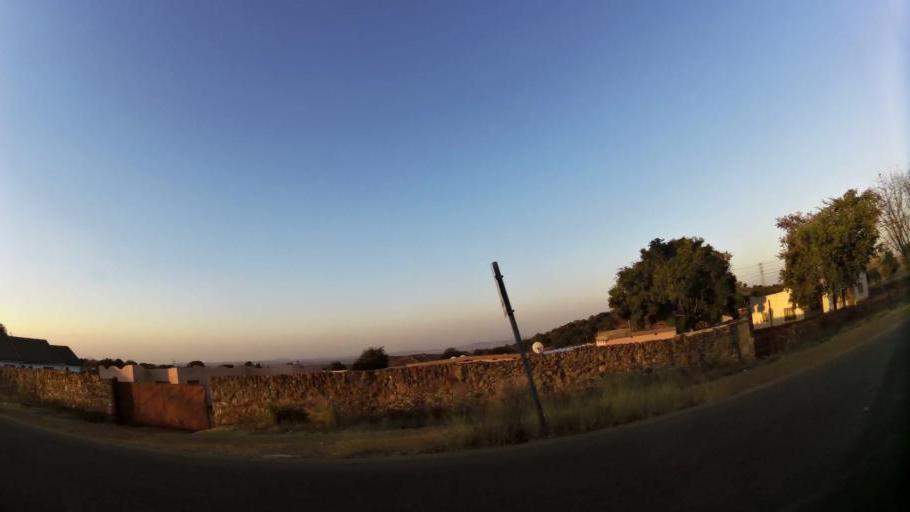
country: ZA
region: North-West
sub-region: Bojanala Platinum District Municipality
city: Rustenburg
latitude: -25.6301
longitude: 27.2007
